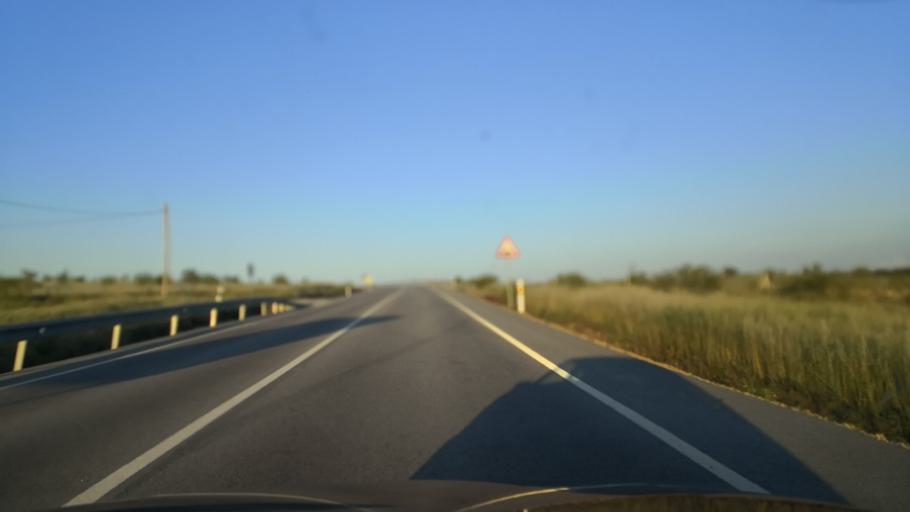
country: ES
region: Extremadura
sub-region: Provincia de Caceres
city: Salorino
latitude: 39.5145
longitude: -7.0539
